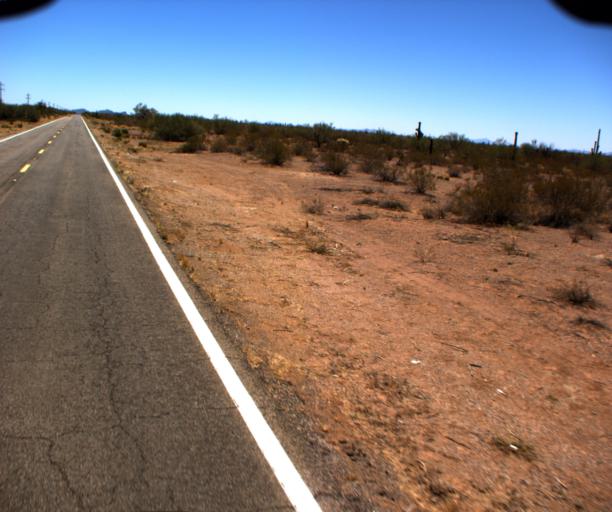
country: US
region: Arizona
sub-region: Pima County
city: Sells
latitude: 32.0871
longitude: -112.0551
